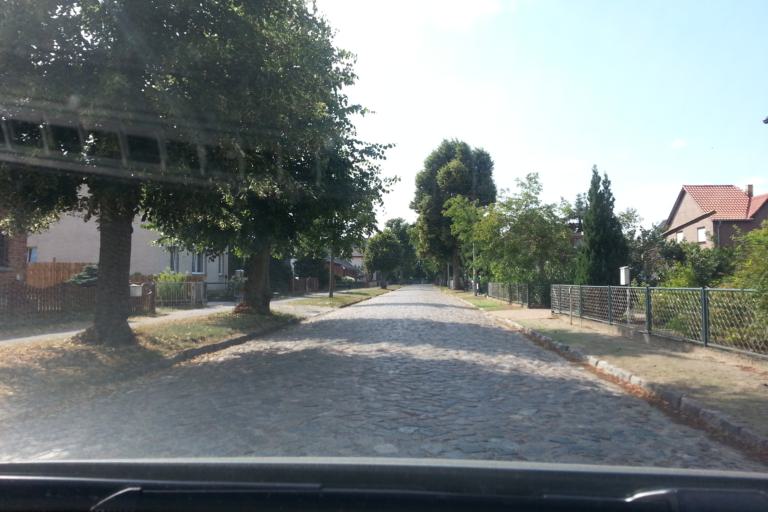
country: DE
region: Mecklenburg-Vorpommern
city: Ferdinandshof
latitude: 53.6291
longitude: 13.8642
